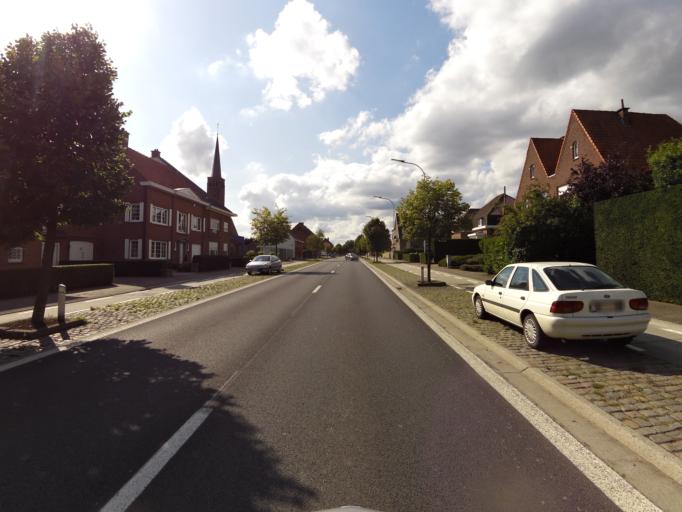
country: BE
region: Flanders
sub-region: Provincie Oost-Vlaanderen
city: Ronse
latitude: 50.7484
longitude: 3.5686
